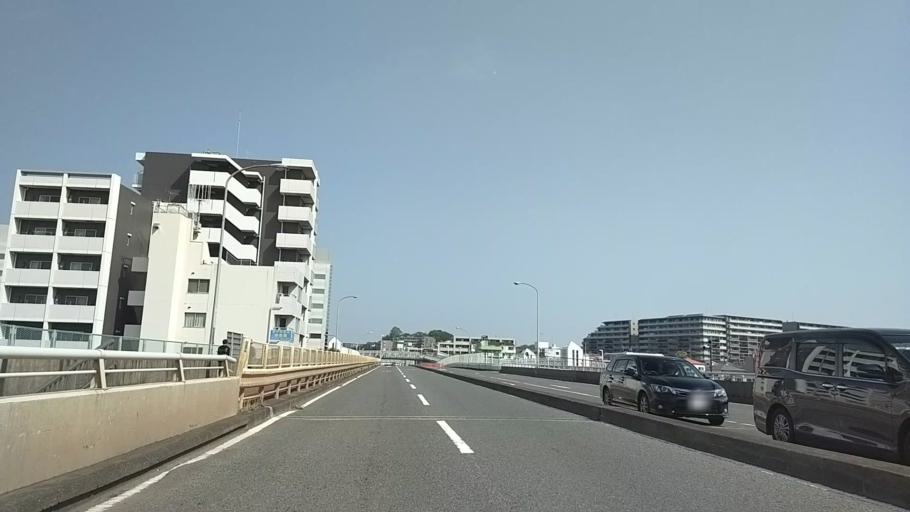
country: JP
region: Kanagawa
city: Yokohama
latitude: 35.4857
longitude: 139.6551
